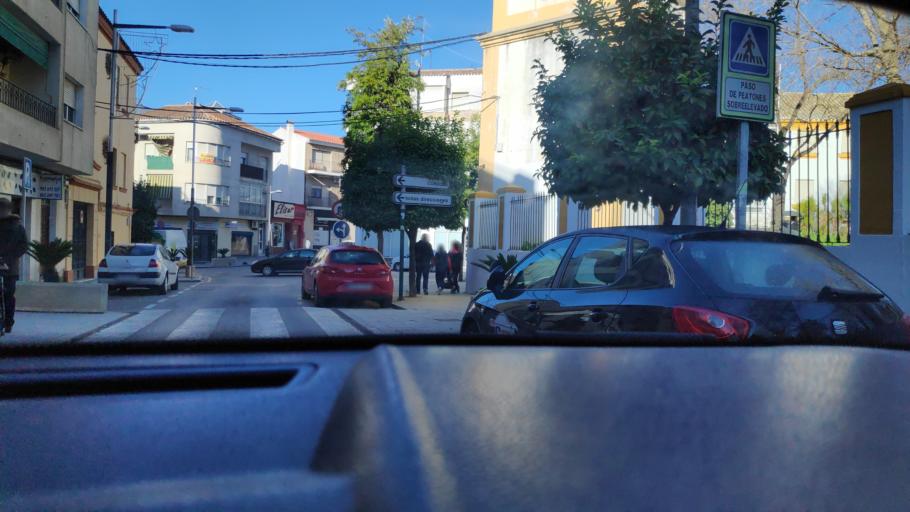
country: ES
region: Andalusia
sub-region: Province of Cordoba
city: Baena
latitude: 37.6166
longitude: -4.3220
